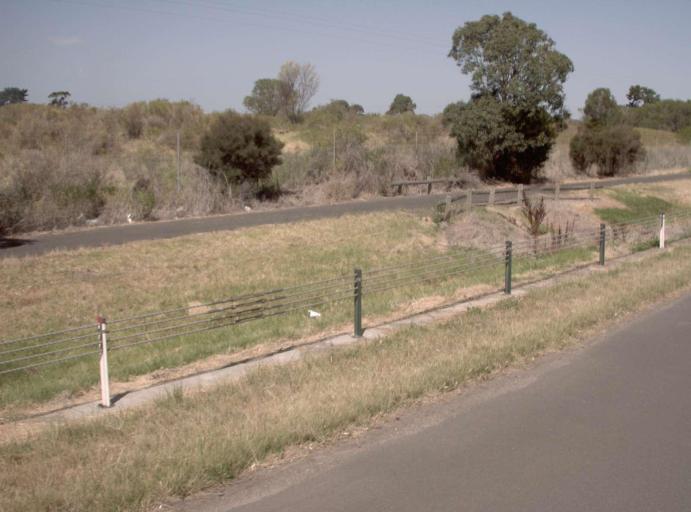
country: AU
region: Victoria
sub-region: Kingston
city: Dingley Village
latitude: -37.9779
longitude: 145.1415
